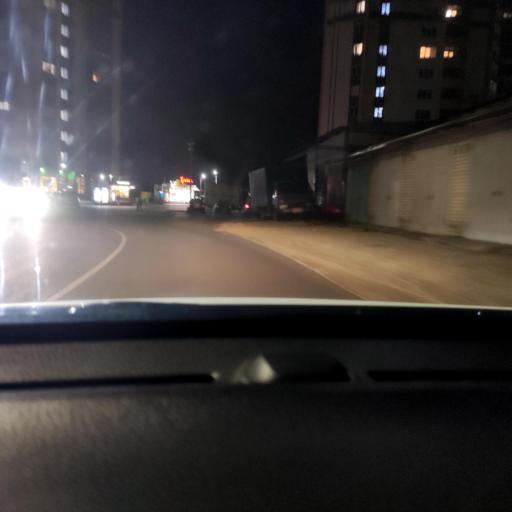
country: RU
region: Voronezj
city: Maslovka
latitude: 51.5896
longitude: 39.2435
